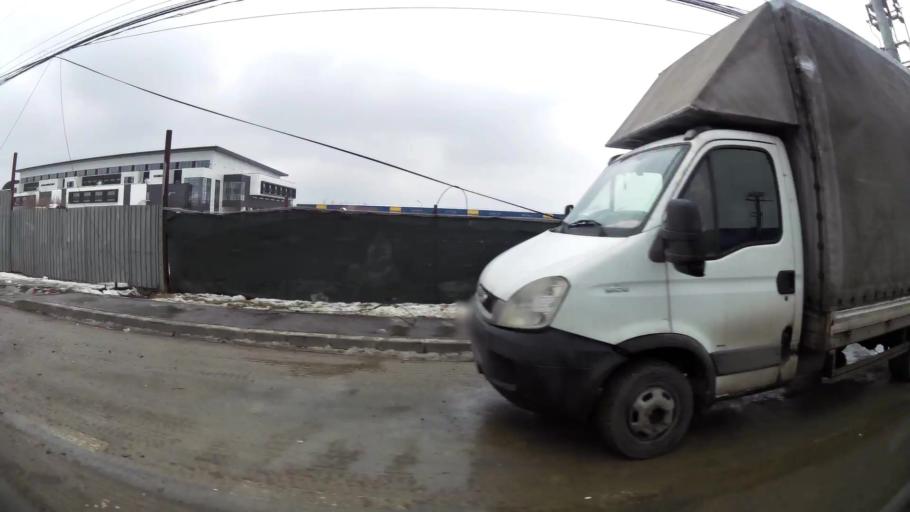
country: RO
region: Ilfov
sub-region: Comuna Otopeni
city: Otopeni
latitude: 44.5428
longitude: 26.0819
